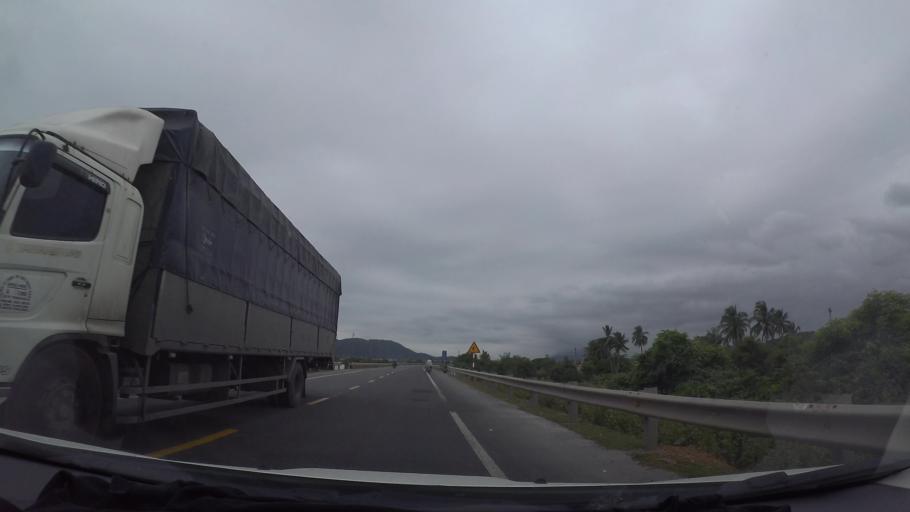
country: VN
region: Da Nang
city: Lien Chieu
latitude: 16.1117
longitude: 108.1049
